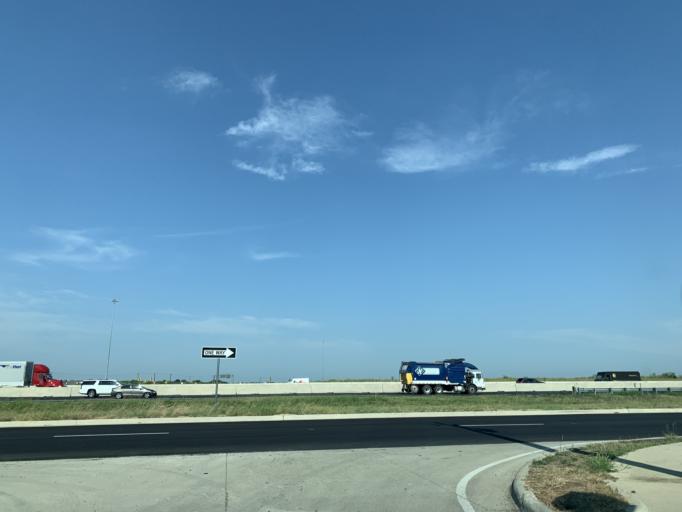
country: US
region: Texas
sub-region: Tarrant County
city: Blue Mound
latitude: 32.8899
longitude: -97.3163
